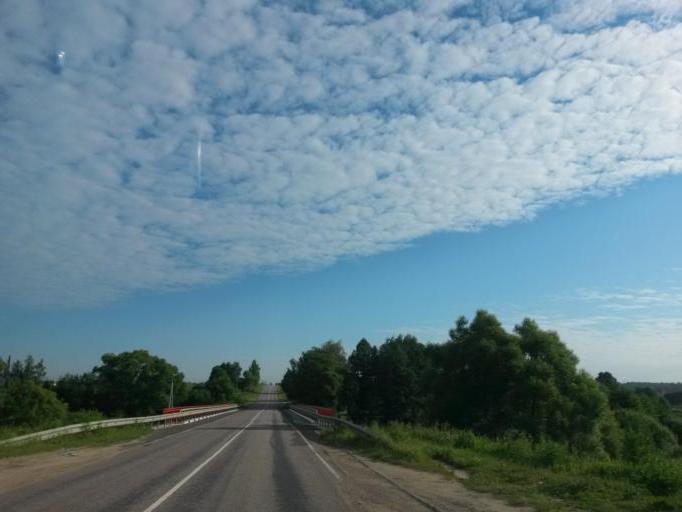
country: RU
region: Moskovskaya
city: Barybino
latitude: 55.2333
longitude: 37.7974
